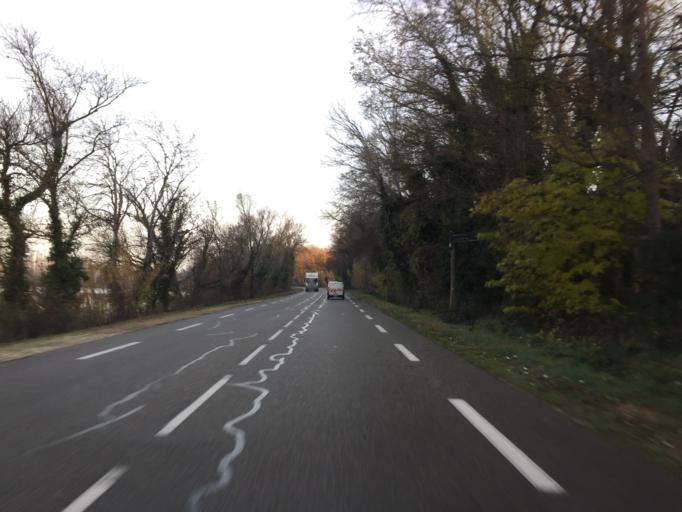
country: FR
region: Languedoc-Roussillon
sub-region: Departement du Gard
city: Montfaucon
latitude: 44.0850
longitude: 4.7619
